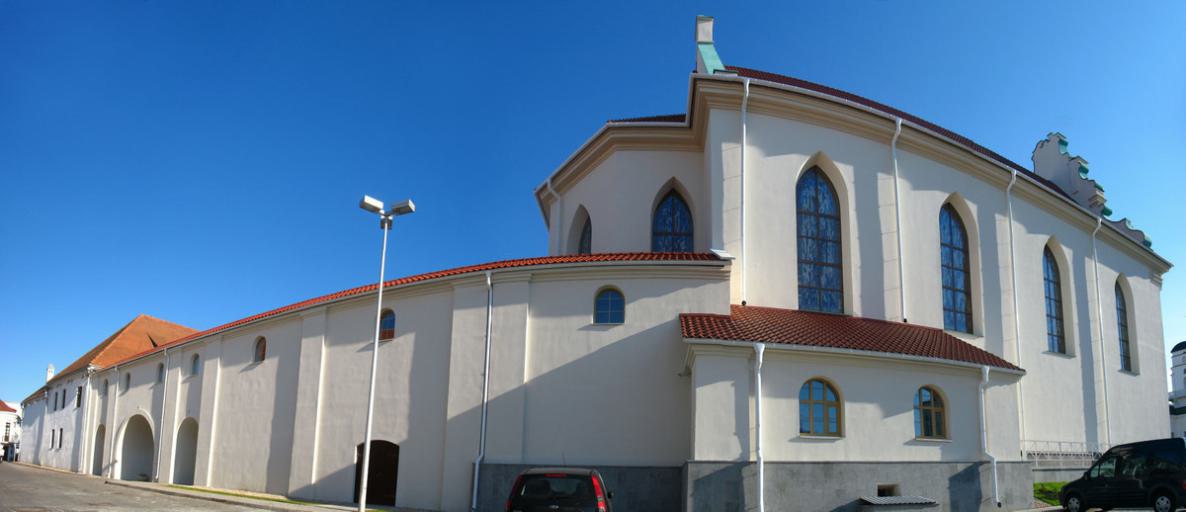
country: BY
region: Minsk
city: Minsk
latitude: 53.9045
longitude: 27.5573
